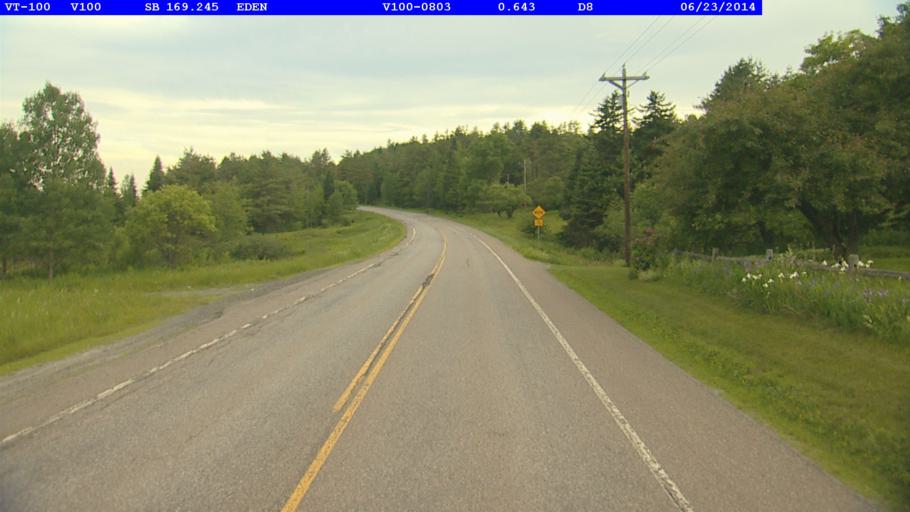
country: US
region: Vermont
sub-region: Lamoille County
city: Hyde Park
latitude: 44.6920
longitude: -72.5852
